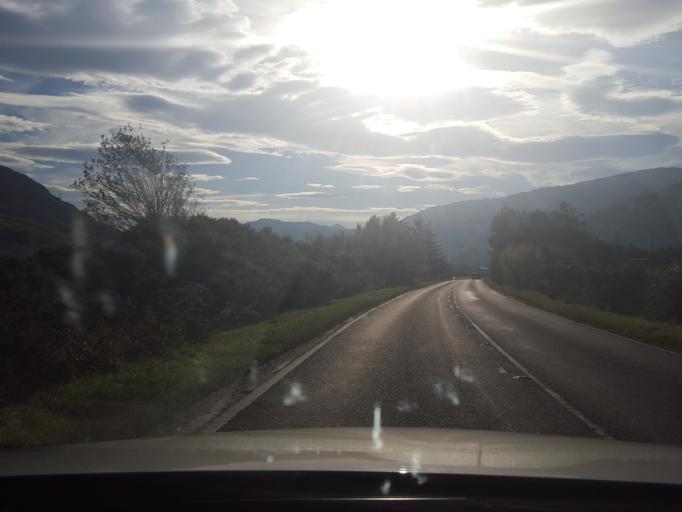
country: GB
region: Scotland
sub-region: Highland
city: Fort William
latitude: 57.2830
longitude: -5.5232
